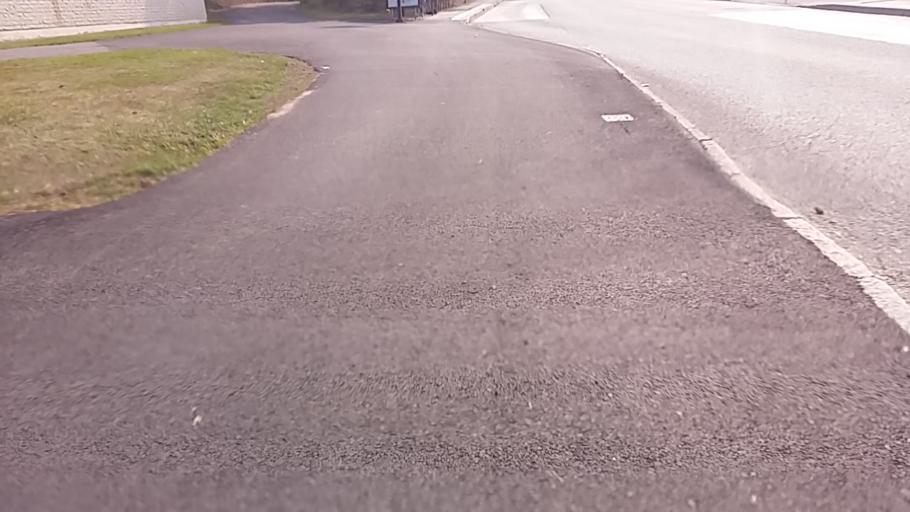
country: SE
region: Joenkoeping
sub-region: Jonkopings Kommun
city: Jonkoping
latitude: 57.7543
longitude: 14.1532
